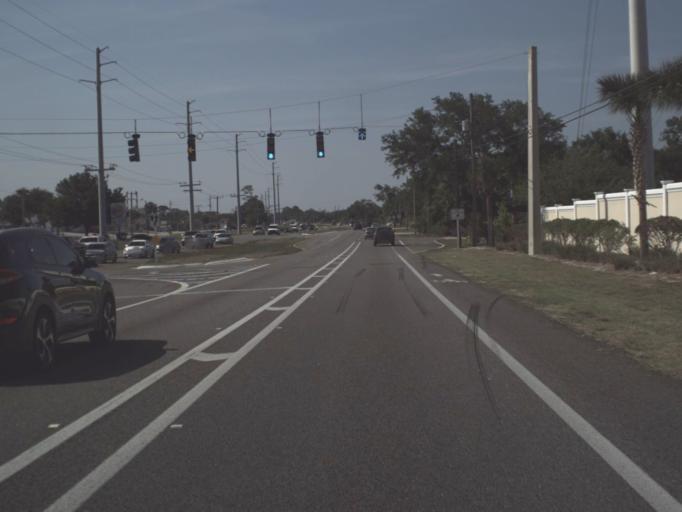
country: US
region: Florida
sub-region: Brevard County
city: Port Saint John
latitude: 28.4712
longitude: -80.7664
